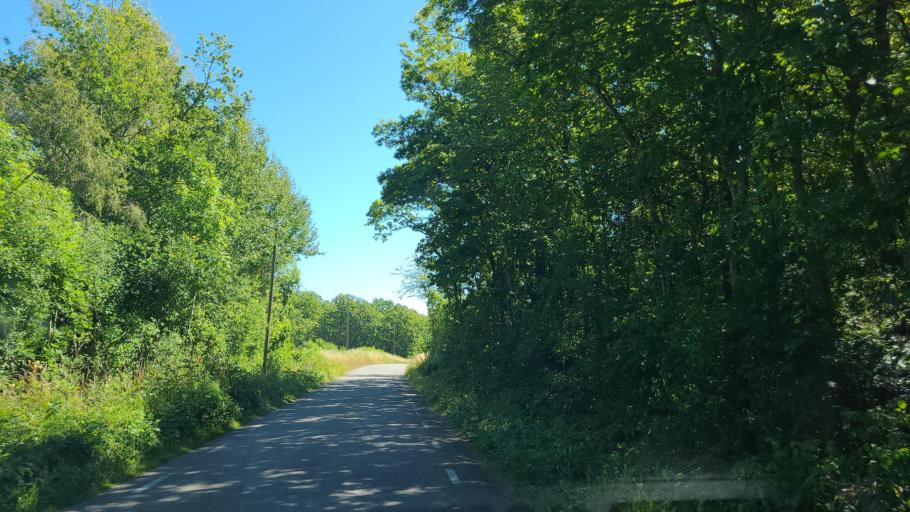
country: SE
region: Kalmar
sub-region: Borgholms Kommun
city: Borgholm
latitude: 56.7617
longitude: 16.6537
